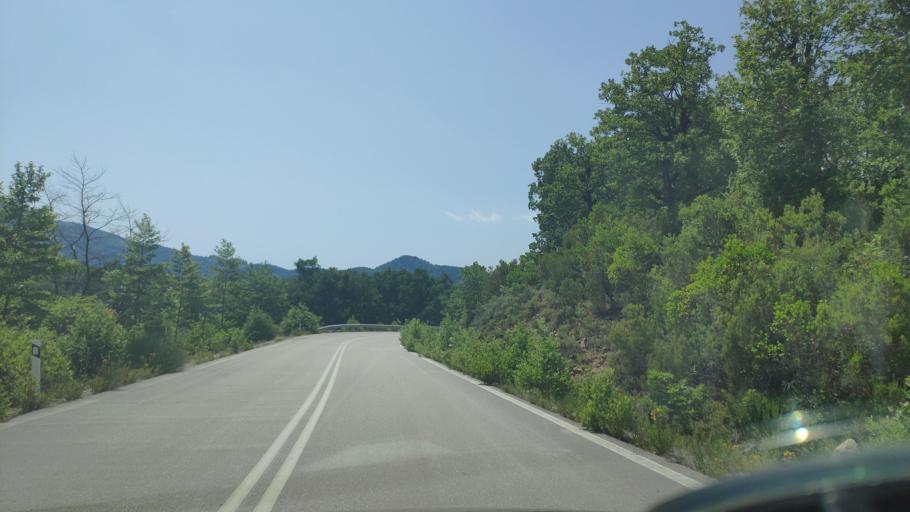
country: GR
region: Epirus
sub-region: Nomos Artas
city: Ano Kalentini
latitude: 39.2791
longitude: 21.3273
